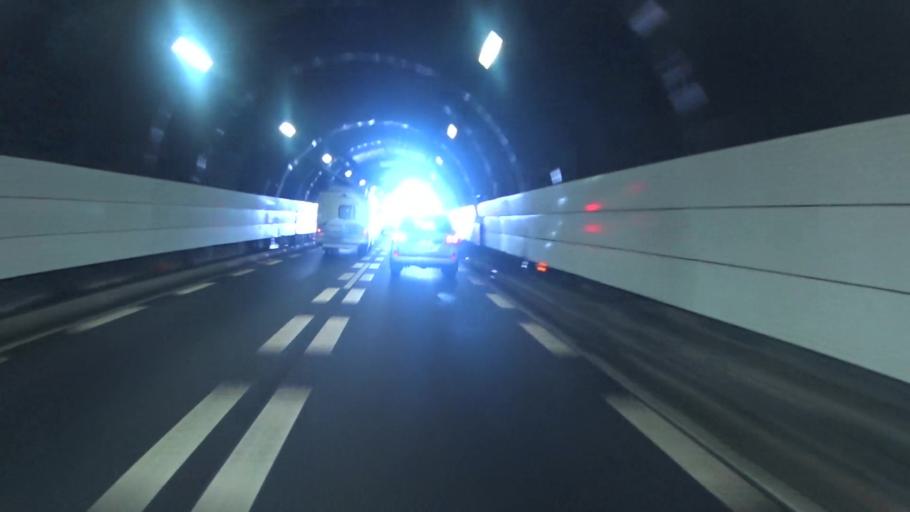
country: JP
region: Shiga Prefecture
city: Otsu-shi
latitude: 34.9982
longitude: 135.8612
